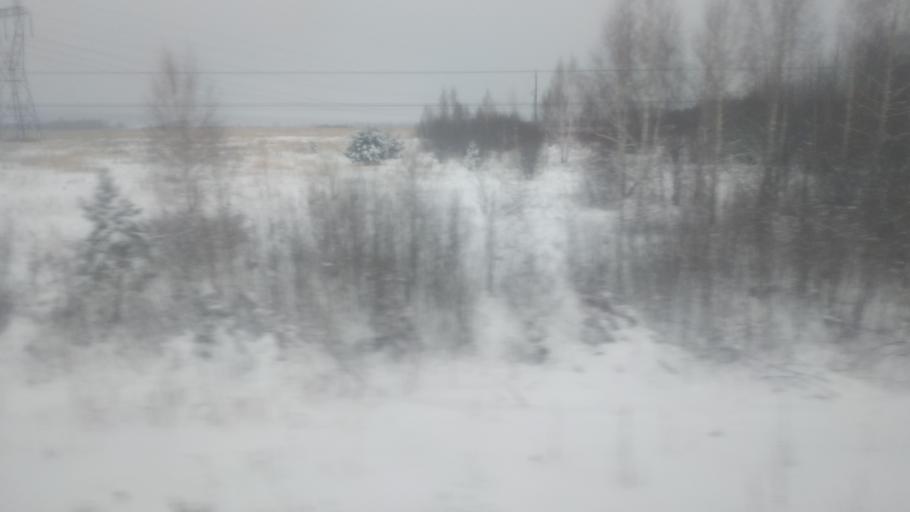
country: RU
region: Bashkortostan
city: Yanaul
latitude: 56.2509
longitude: 54.6837
